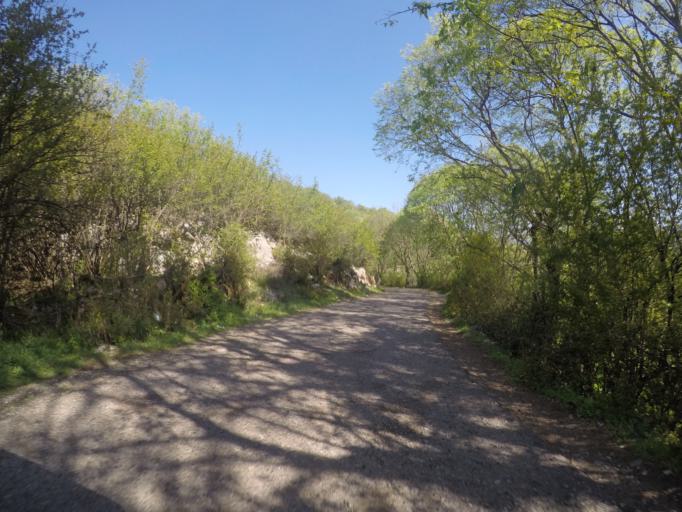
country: ME
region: Danilovgrad
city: Danilovgrad
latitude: 42.5337
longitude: 19.0891
